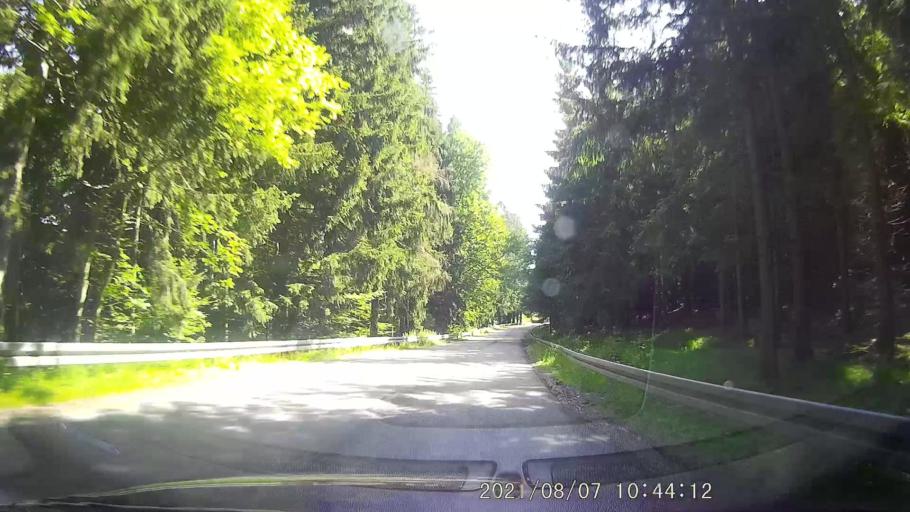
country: PL
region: Lower Silesian Voivodeship
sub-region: Powiat klodzki
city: Duszniki-Zdroj
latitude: 50.3305
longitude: 16.4042
